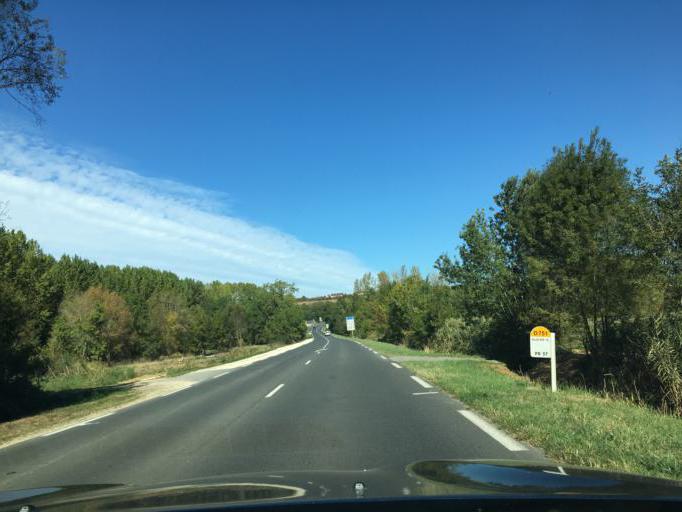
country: FR
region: Centre
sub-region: Departement d'Indre-et-Loire
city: Azay-le-Rideau
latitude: 47.2582
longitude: 0.4566
